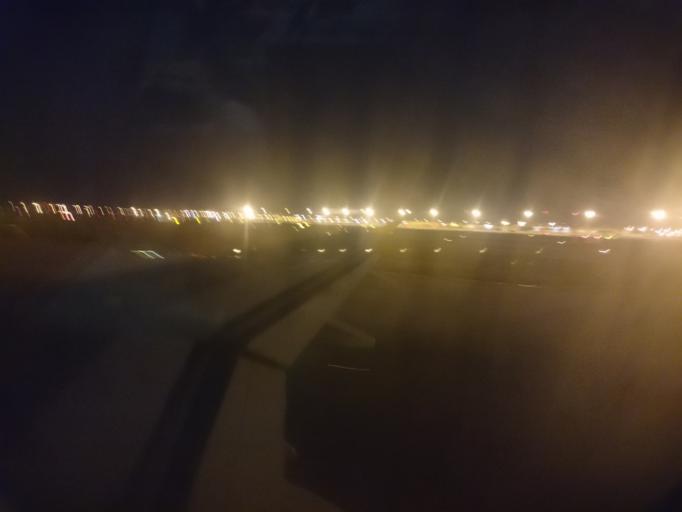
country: ES
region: Catalonia
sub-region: Provincia de Barcelona
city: El Prat de Llobregat
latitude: 41.2953
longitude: 2.0779
